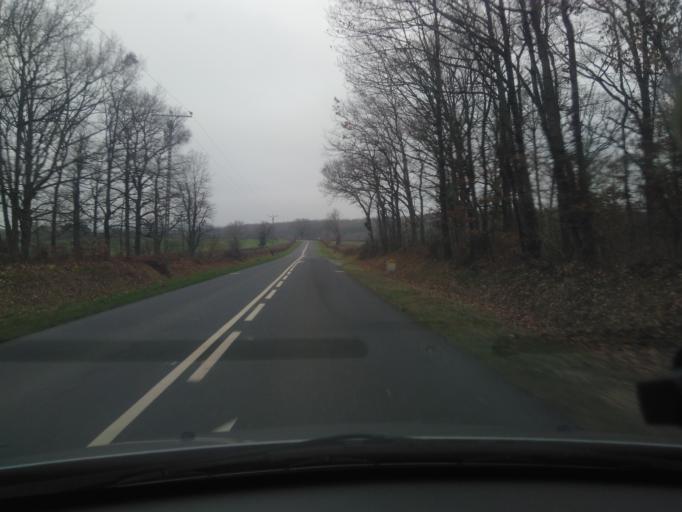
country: FR
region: Centre
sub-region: Departement du Cher
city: Chateaumeillant
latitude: 46.6389
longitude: 2.1024
